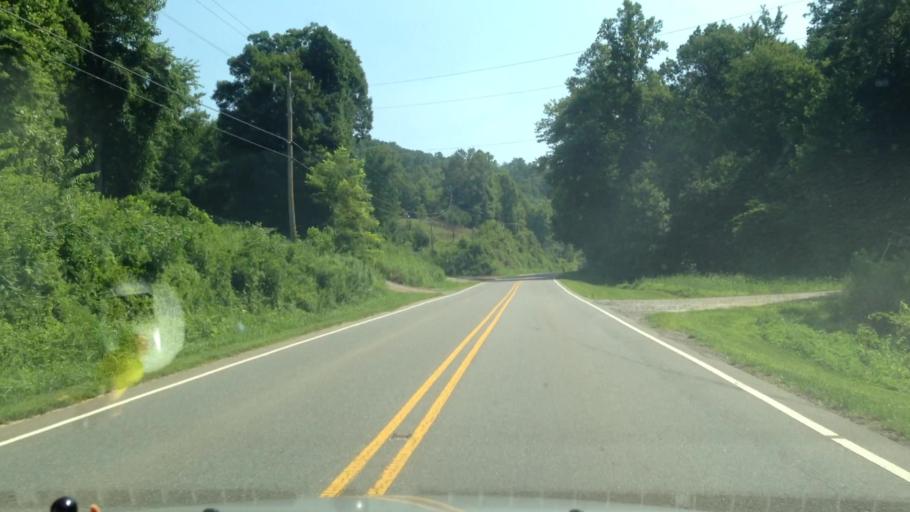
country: US
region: North Carolina
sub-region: Surry County
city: Flat Rock
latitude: 36.5340
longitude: -80.5231
